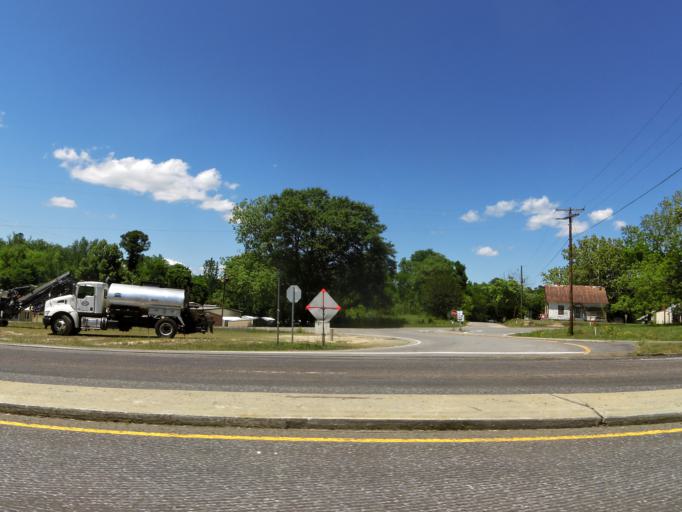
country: US
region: South Carolina
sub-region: Aiken County
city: Warrenville
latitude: 33.5538
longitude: -81.8126
